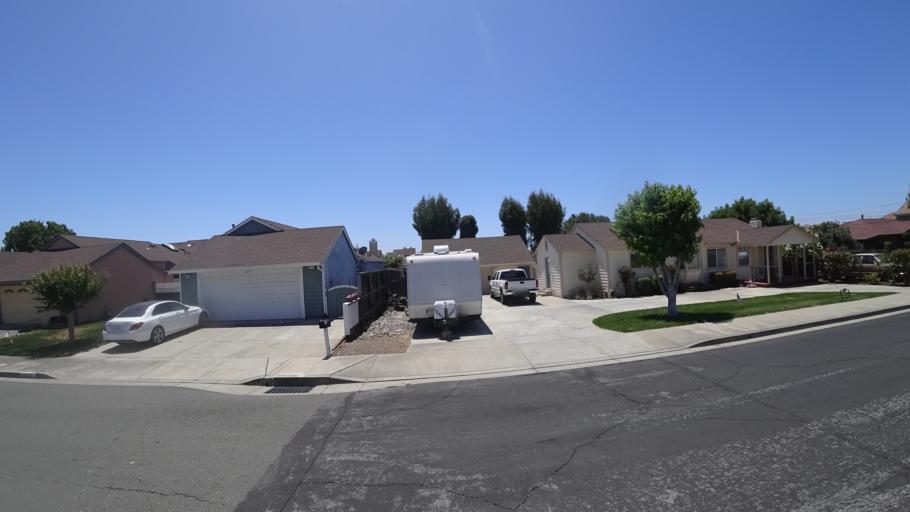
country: US
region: California
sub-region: Alameda County
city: Union City
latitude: 37.6269
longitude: -122.0563
